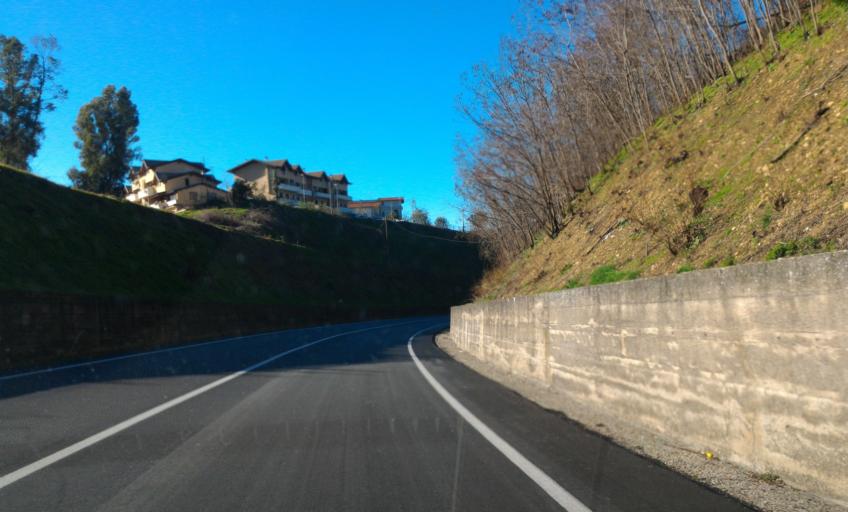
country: IT
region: Calabria
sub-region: Provincia di Cosenza
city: Rovito
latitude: 39.2969
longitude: 16.3072
